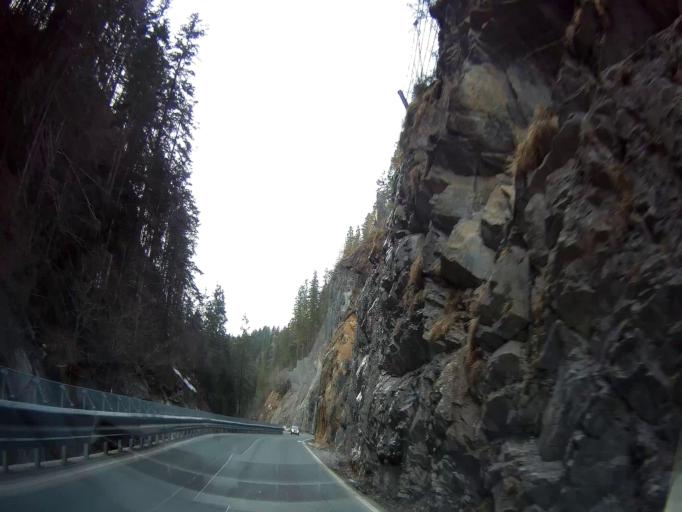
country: AT
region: Salzburg
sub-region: Politischer Bezirk Hallein
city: Abtenau
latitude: 47.5432
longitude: 13.4209
